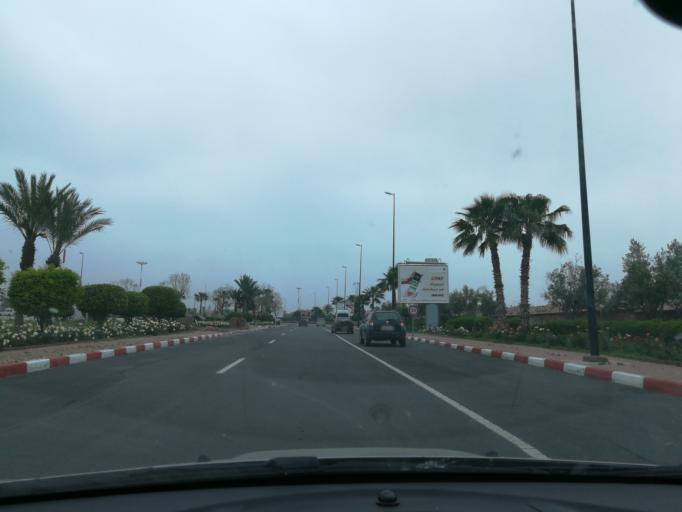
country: MA
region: Marrakech-Tensift-Al Haouz
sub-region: Marrakech
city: Marrakesh
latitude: 31.6002
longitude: -8.0283
